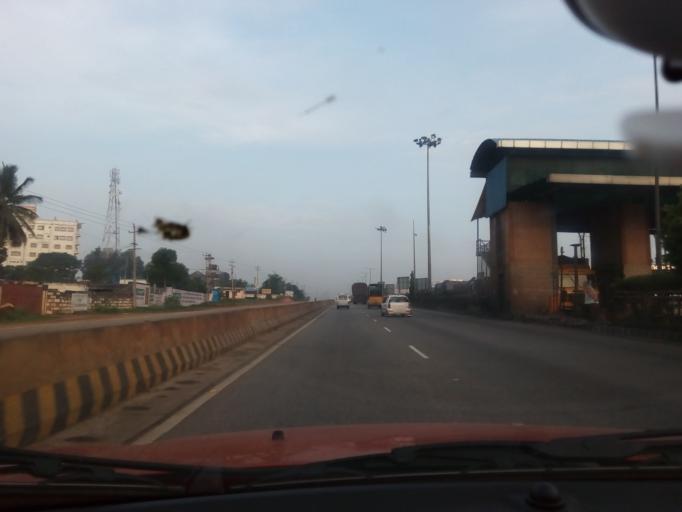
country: IN
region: Karnataka
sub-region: Bangalore Rural
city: Nelamangala
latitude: 13.0904
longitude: 77.4003
